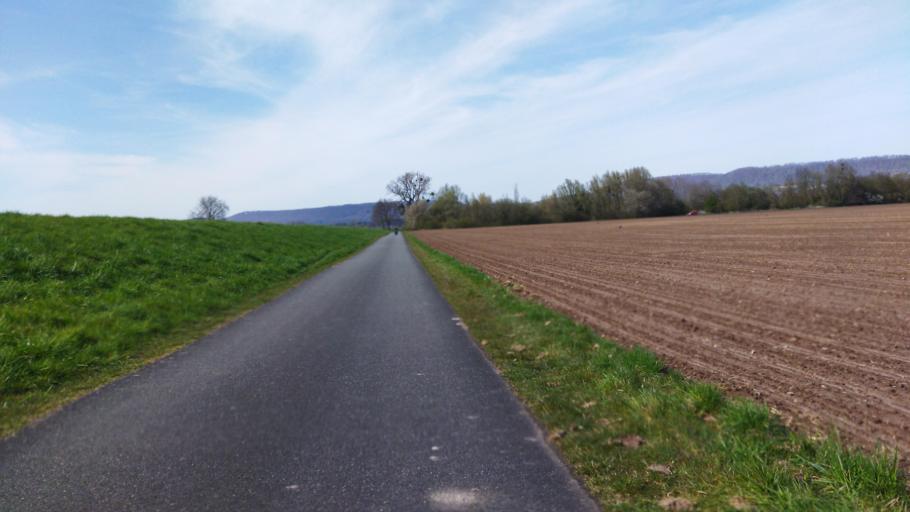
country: DE
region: Lower Saxony
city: Hessisch Oldendorf
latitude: 52.1524
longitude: 9.2737
